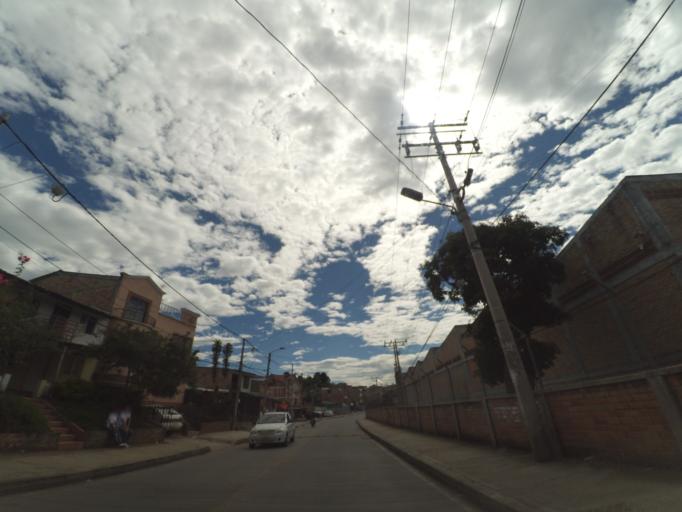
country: CO
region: Cauca
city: Popayan
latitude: 2.4626
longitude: -76.6529
